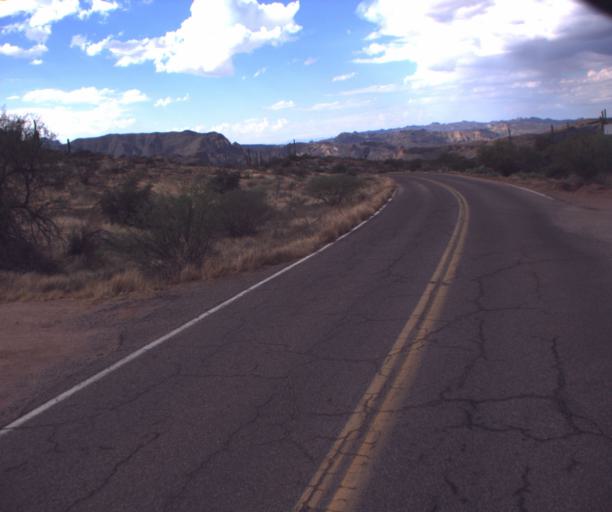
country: US
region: Arizona
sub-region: Pinal County
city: Apache Junction
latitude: 33.5444
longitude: -111.3377
